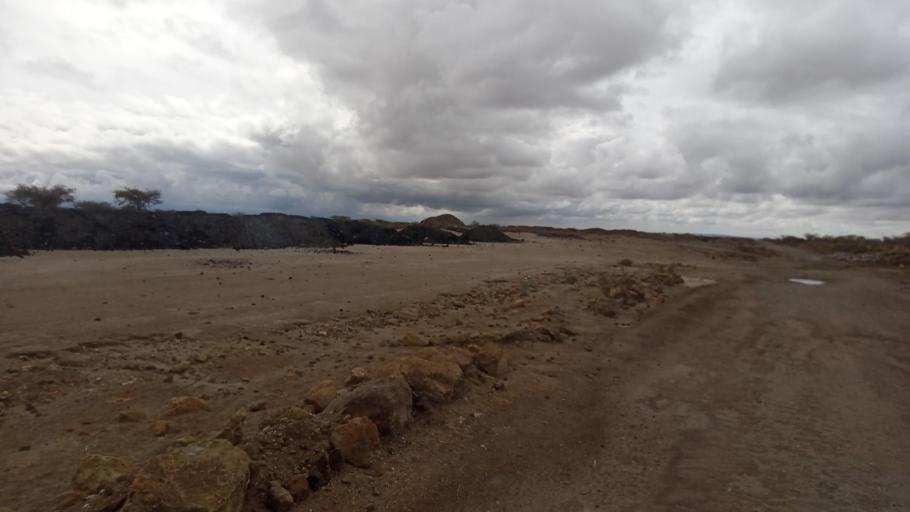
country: ET
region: Oromiya
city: Ziway
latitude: 7.5677
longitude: 38.6742
